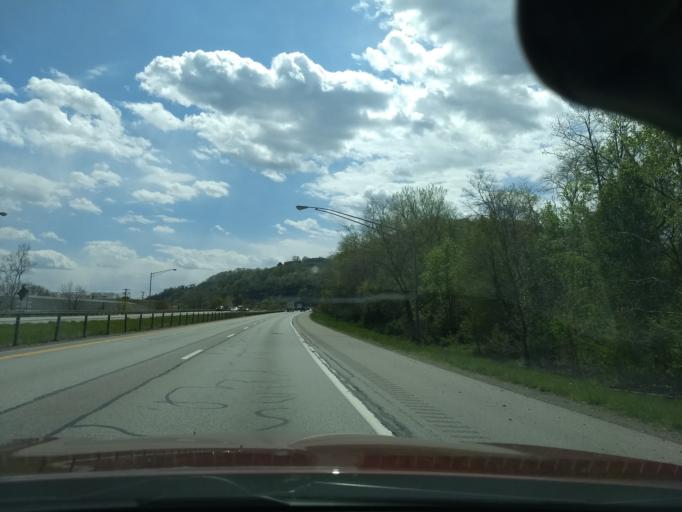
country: US
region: Pennsylvania
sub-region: Allegheny County
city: Oakmont
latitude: 40.5366
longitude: -79.8442
